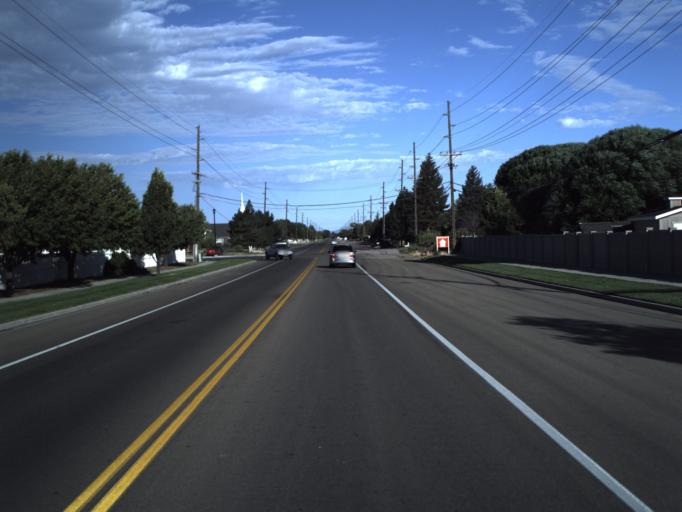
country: US
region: Utah
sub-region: Utah County
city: Spanish Fork
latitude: 40.0958
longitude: -111.6150
